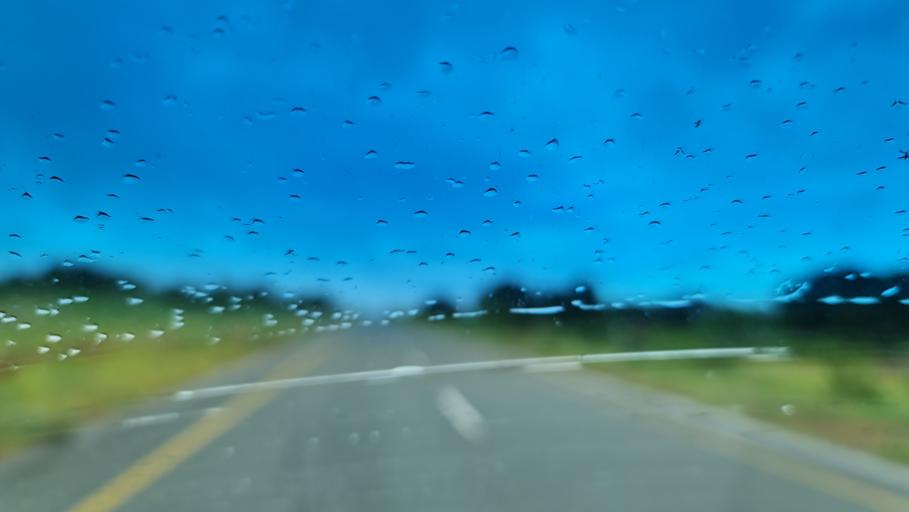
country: MZ
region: Nampula
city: Nampula
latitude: -15.5226
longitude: 39.3331
